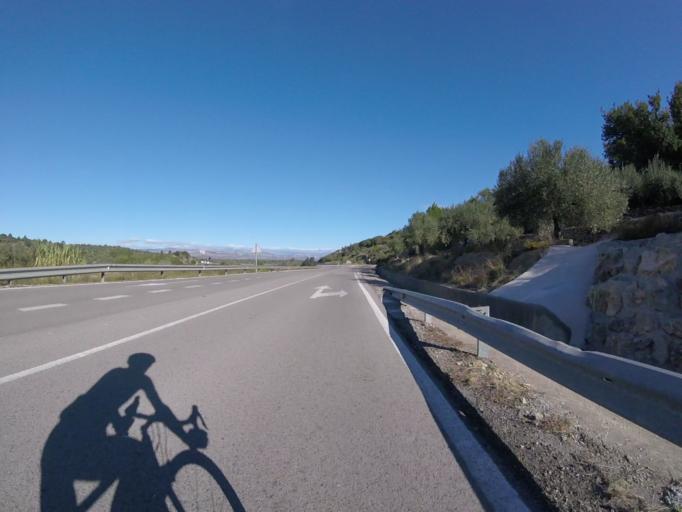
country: ES
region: Valencia
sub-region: Provincia de Castello
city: Cervera del Maestre
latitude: 40.4640
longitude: 0.2515
